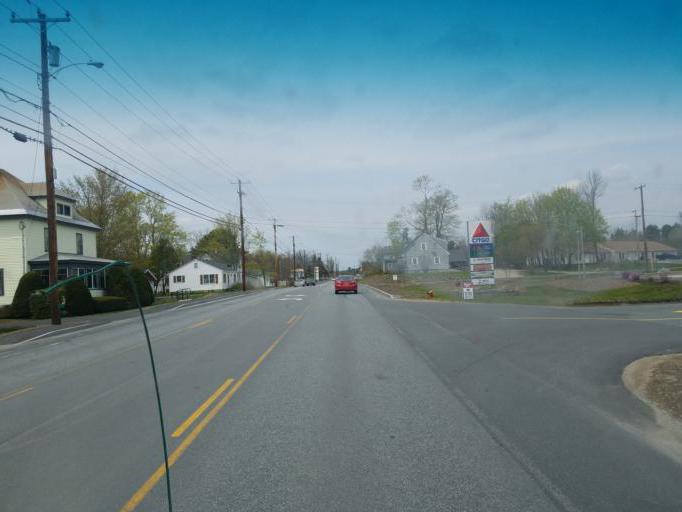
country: US
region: Maine
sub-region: Hancock County
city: Ellsworth
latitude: 44.5582
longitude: -68.4347
